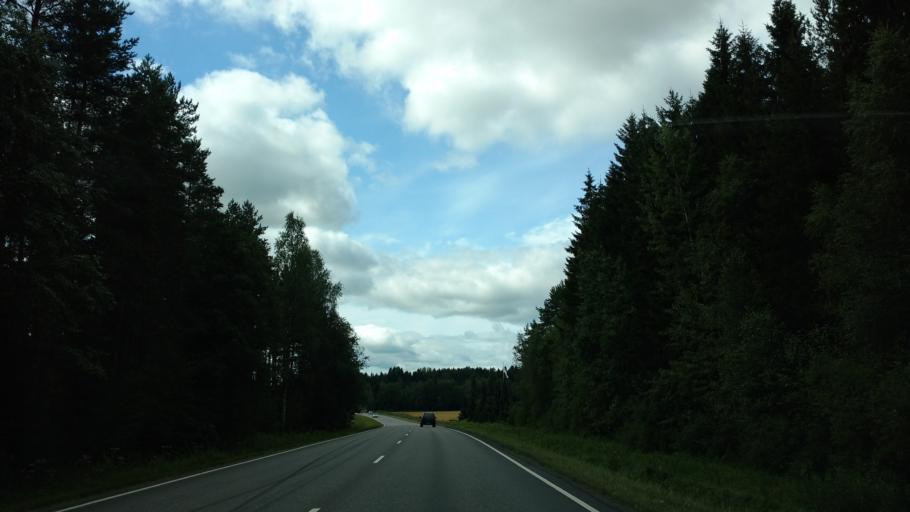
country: FI
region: Varsinais-Suomi
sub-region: Salo
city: Pernioe
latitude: 60.1972
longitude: 23.0745
